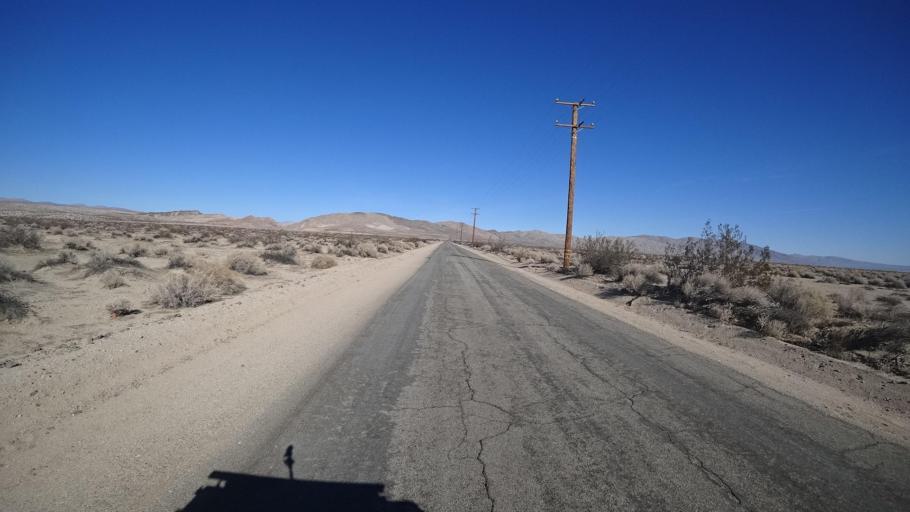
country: US
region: California
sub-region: Kern County
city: California City
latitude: 35.3115
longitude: -117.9504
